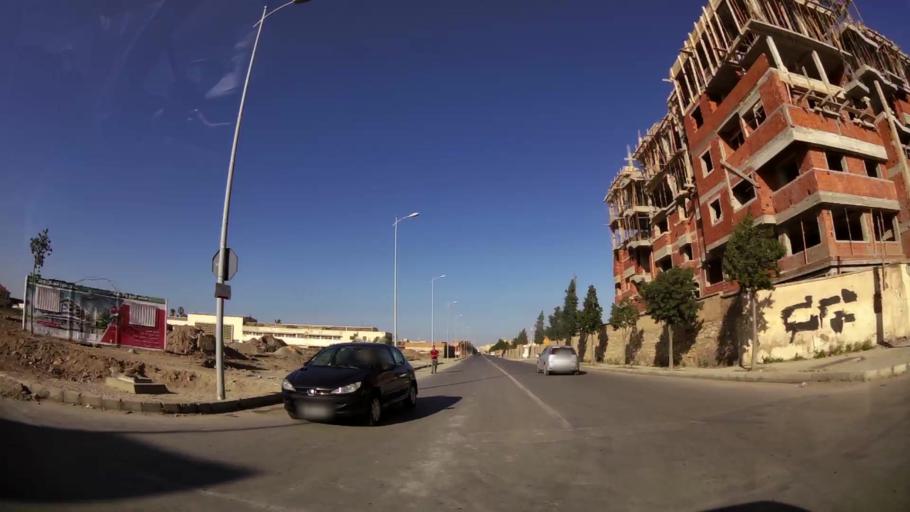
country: MA
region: Oriental
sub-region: Oujda-Angad
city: Oujda
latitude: 34.6959
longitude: -1.9090
